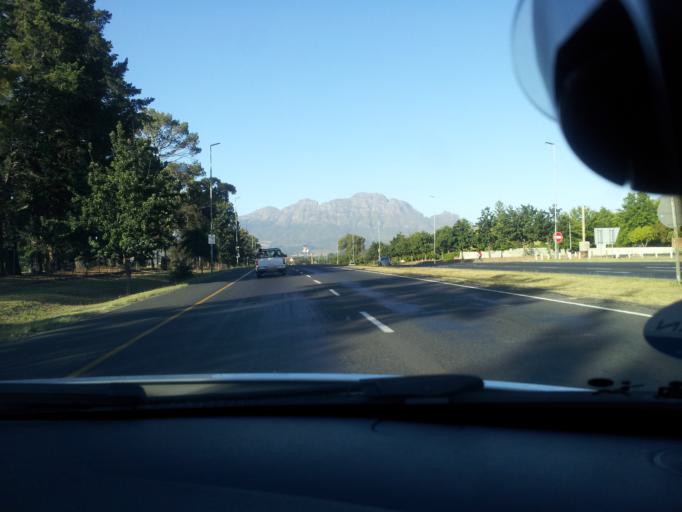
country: ZA
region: Western Cape
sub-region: Cape Winelands District Municipality
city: Stellenbosch
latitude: -33.9627
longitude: 18.8508
